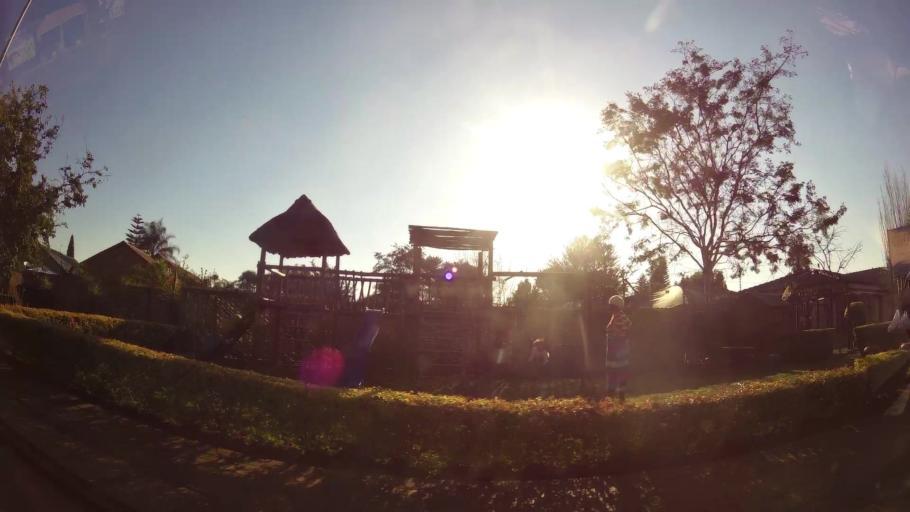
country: ZA
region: Gauteng
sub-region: City of Tshwane Metropolitan Municipality
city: Centurion
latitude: -25.8785
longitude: 28.1513
